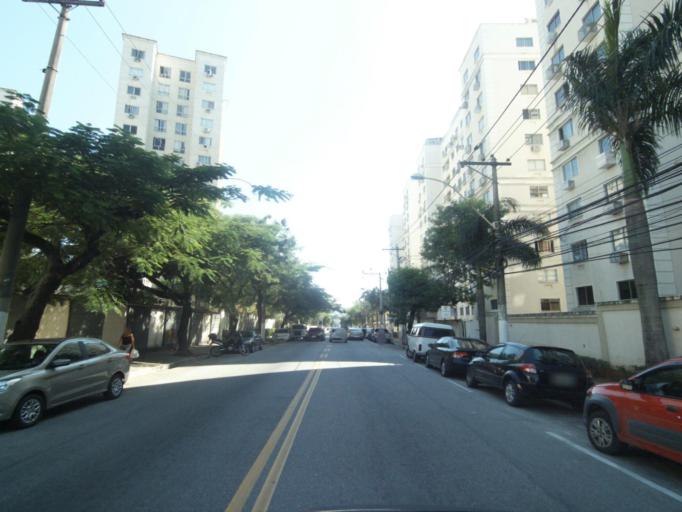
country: BR
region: Rio de Janeiro
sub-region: Niteroi
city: Niteroi
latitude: -22.8630
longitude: -43.0967
